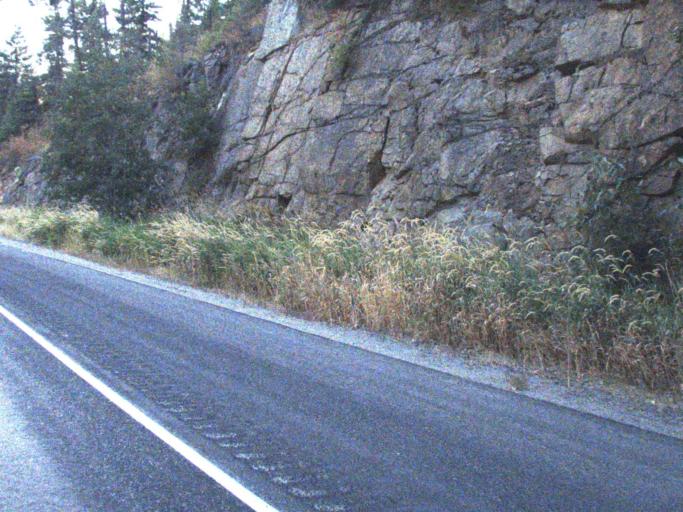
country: US
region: Washington
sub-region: Spokane County
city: Deer Park
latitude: 48.0875
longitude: -117.3260
